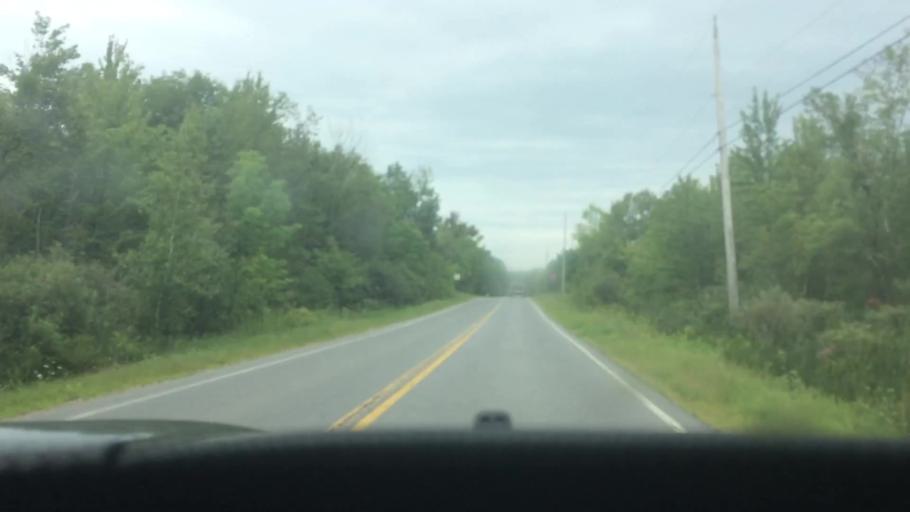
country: US
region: New York
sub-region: St. Lawrence County
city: Canton
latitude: 44.5059
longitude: -75.2127
